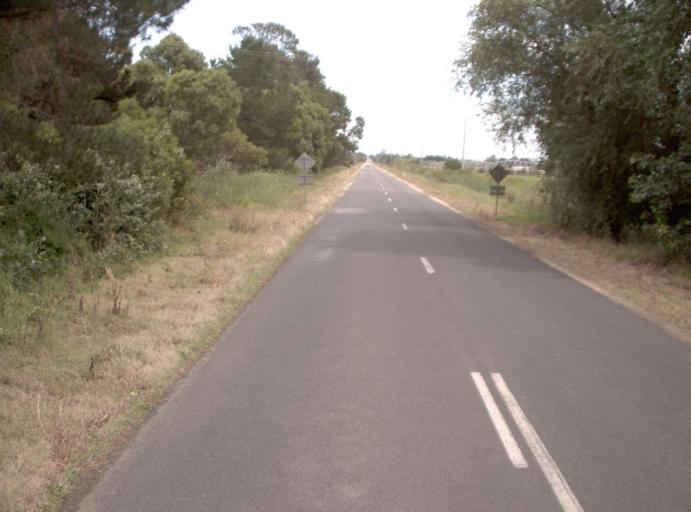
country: AU
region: Victoria
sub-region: Wellington
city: Sale
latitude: -37.9811
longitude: 147.0639
